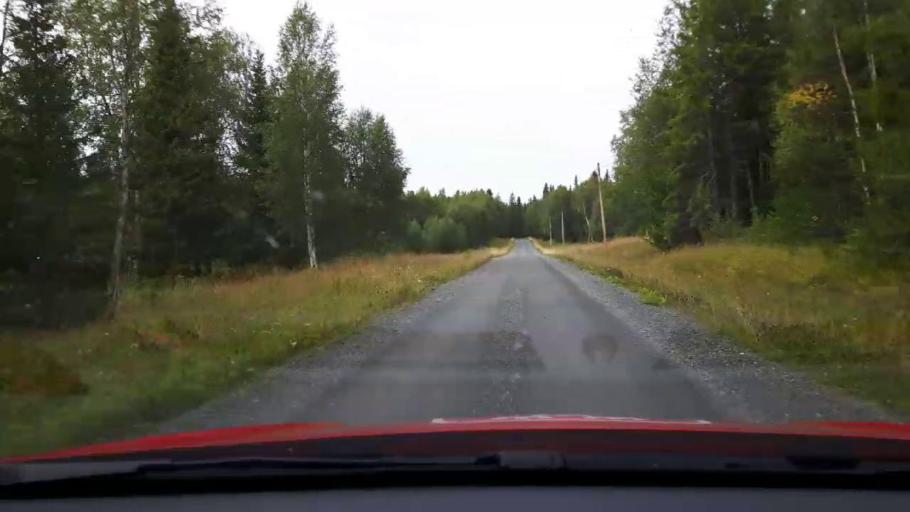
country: SE
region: Jaemtland
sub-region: Are Kommun
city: Are
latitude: 63.7714
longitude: 13.0848
